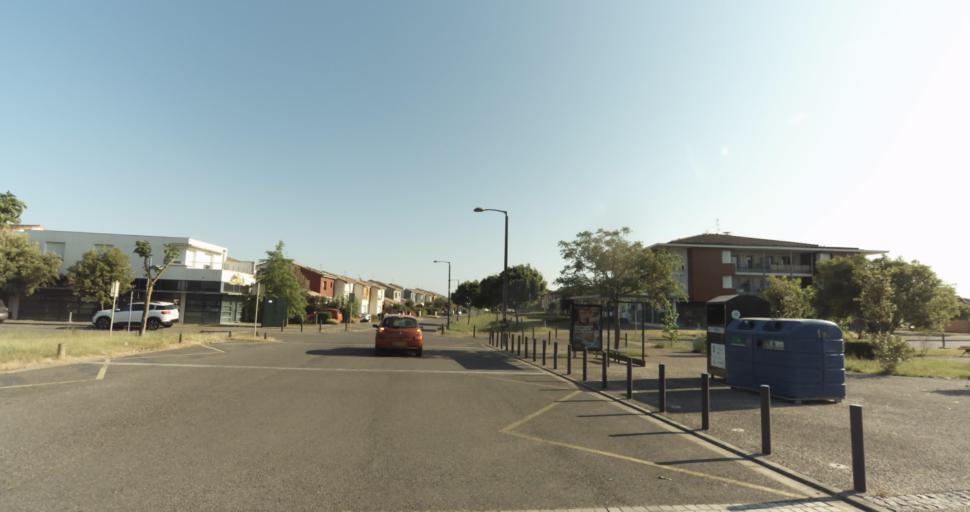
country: FR
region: Midi-Pyrenees
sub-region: Departement de la Haute-Garonne
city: La Salvetat-Saint-Gilles
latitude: 43.5721
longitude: 1.2438
